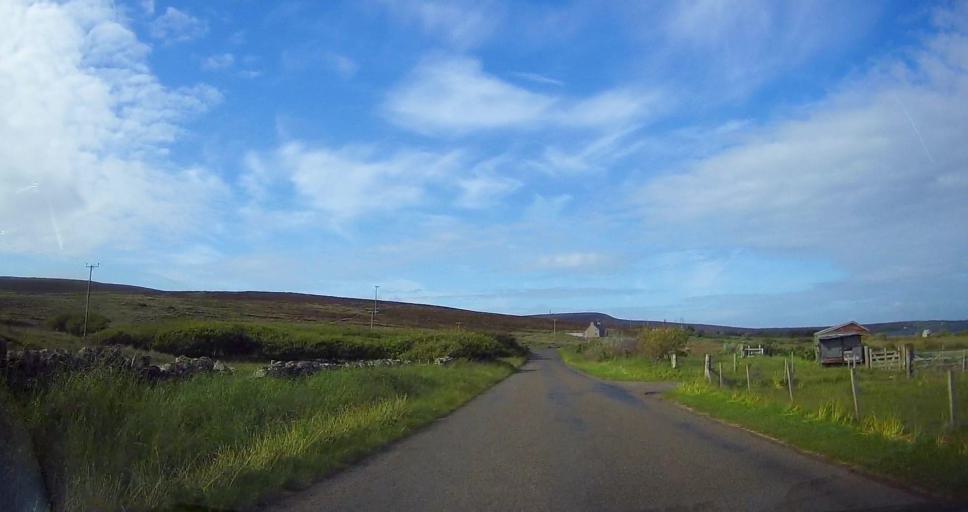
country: GB
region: Scotland
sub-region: Orkney Islands
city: Stromness
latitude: 58.7897
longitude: -3.2589
